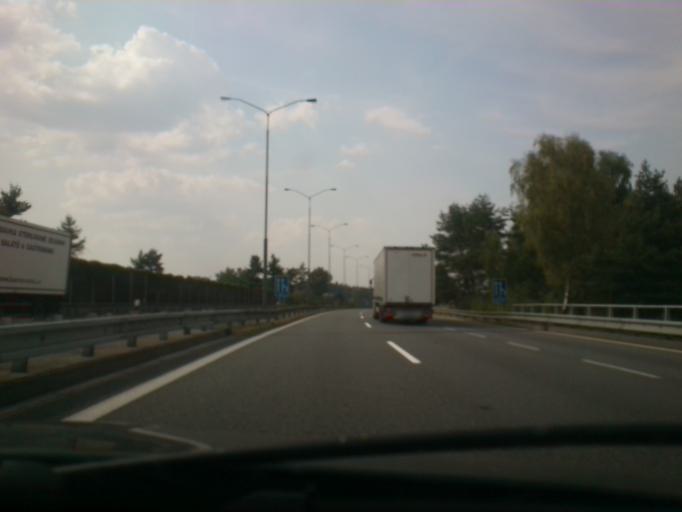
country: CZ
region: Central Bohemia
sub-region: Okres Praha-Vychod
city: Mnichovice
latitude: 49.9137
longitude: 14.7130
